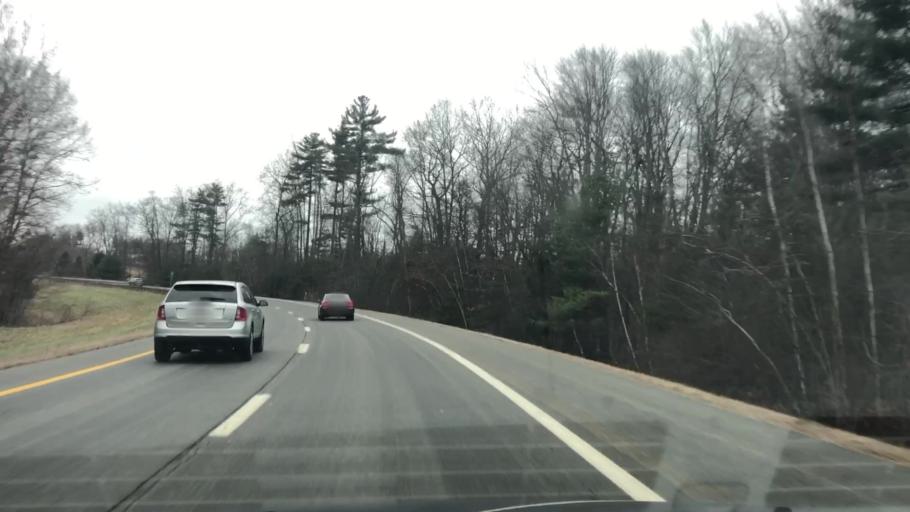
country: US
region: New Hampshire
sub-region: Hillsborough County
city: Hudson
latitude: 42.7202
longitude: -71.4517
